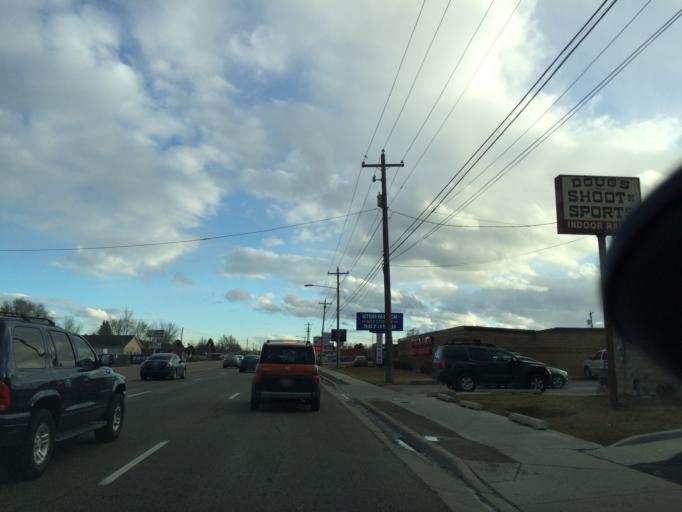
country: US
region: Utah
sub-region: Salt Lake County
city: Taylorsville
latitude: 40.6621
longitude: -111.9390
